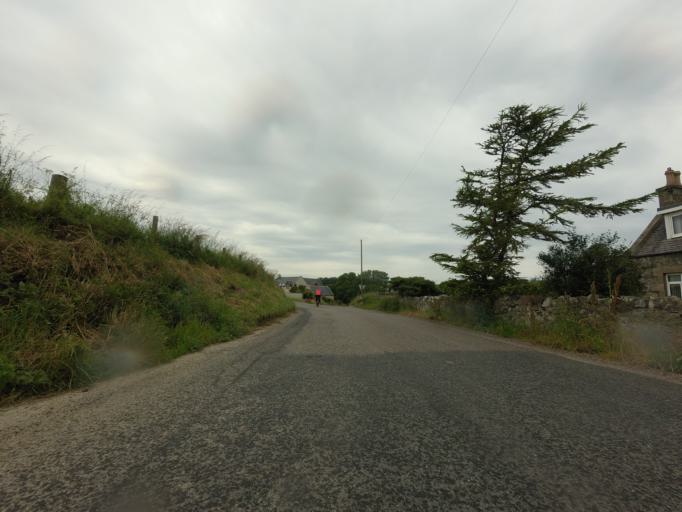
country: GB
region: Scotland
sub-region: Aberdeenshire
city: Portsoy
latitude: 57.6770
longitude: -2.6518
